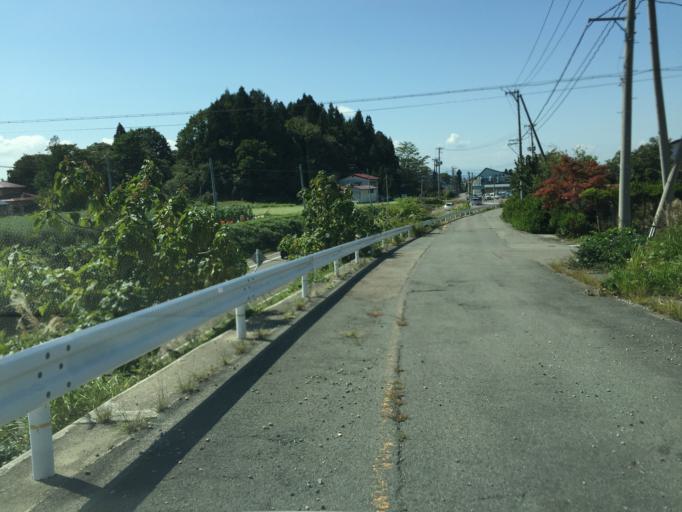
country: JP
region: Fukushima
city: Inawashiro
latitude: 37.5566
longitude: 140.0068
